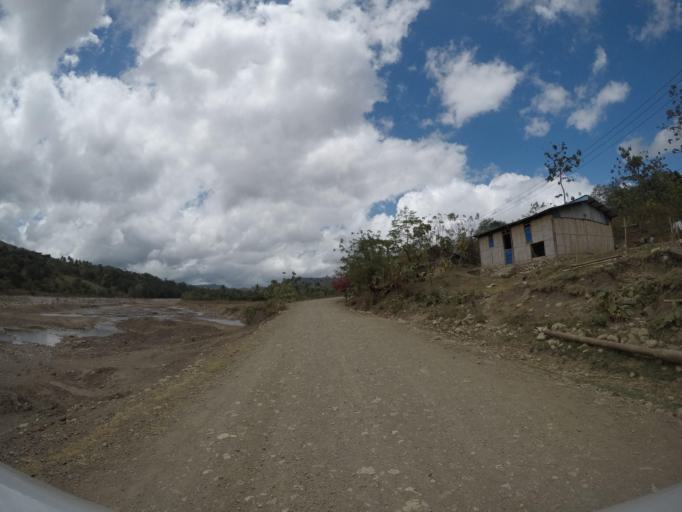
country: TL
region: Lautem
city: Lospalos
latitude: -8.5050
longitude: 126.8317
